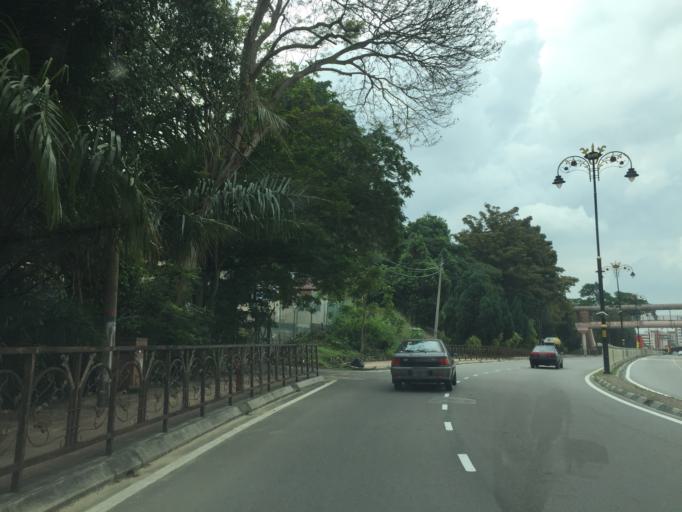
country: MY
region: Selangor
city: Klang
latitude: 3.0381
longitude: 101.4460
